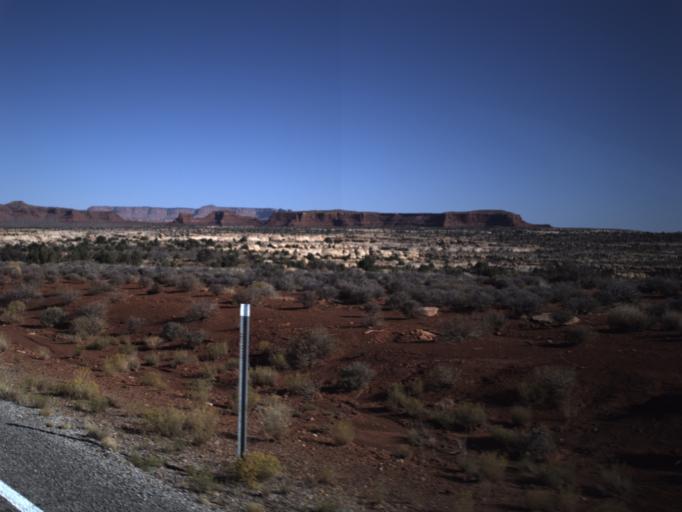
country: US
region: Utah
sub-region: San Juan County
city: Blanding
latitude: 37.7843
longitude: -110.2941
